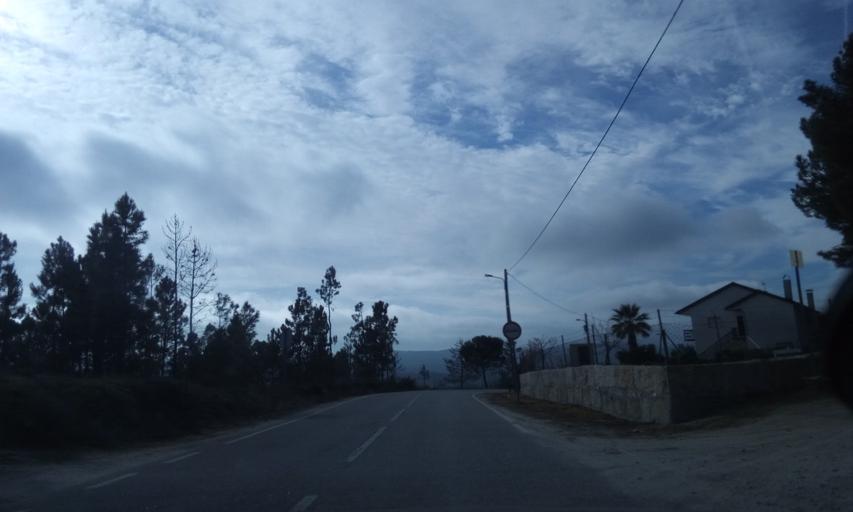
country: PT
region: Guarda
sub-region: Aguiar da Beira
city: Aguiar da Beira
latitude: 40.7415
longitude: -7.5546
